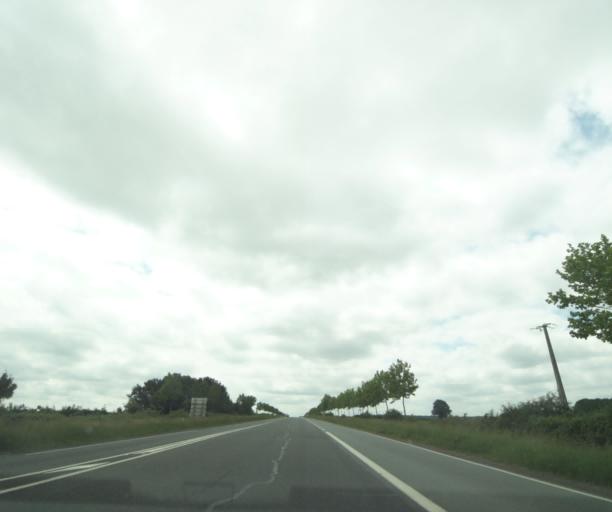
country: FR
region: Poitou-Charentes
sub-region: Departement des Deux-Sevres
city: Saint-Varent
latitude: 46.8466
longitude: -0.2088
